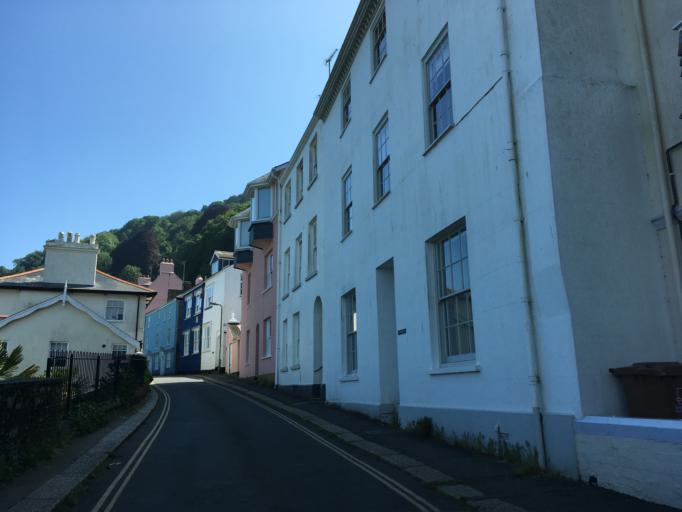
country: GB
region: England
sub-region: Devon
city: Dartmouth
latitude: 50.3470
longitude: -3.5778
